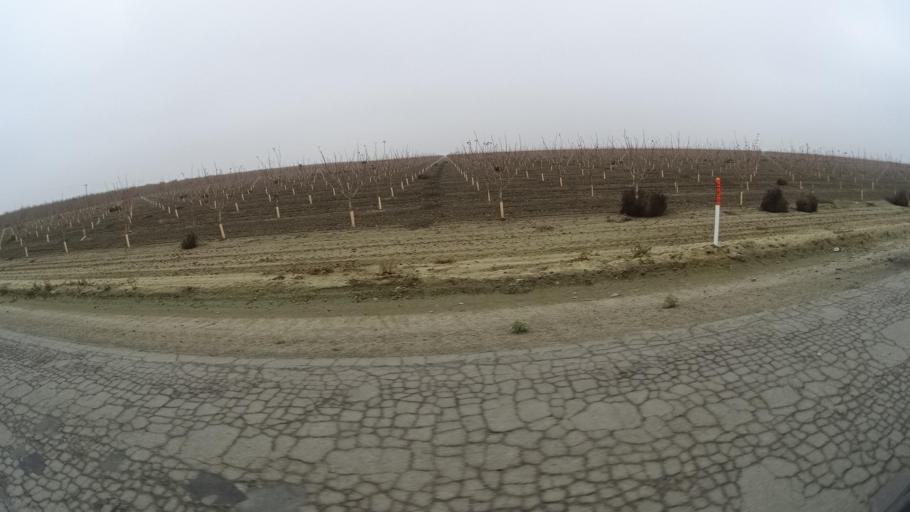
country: US
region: California
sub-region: Kern County
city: Wasco
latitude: 35.6971
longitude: -119.4017
